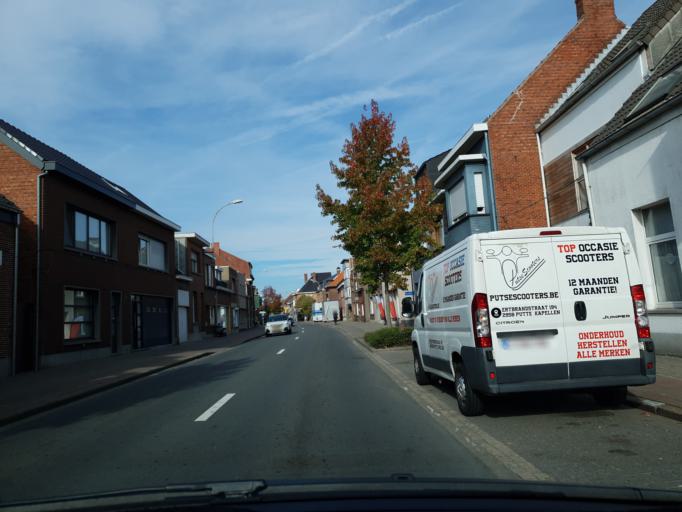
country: BE
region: Flanders
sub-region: Provincie Antwerpen
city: Stabroek
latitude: 51.3524
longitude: 4.3973
